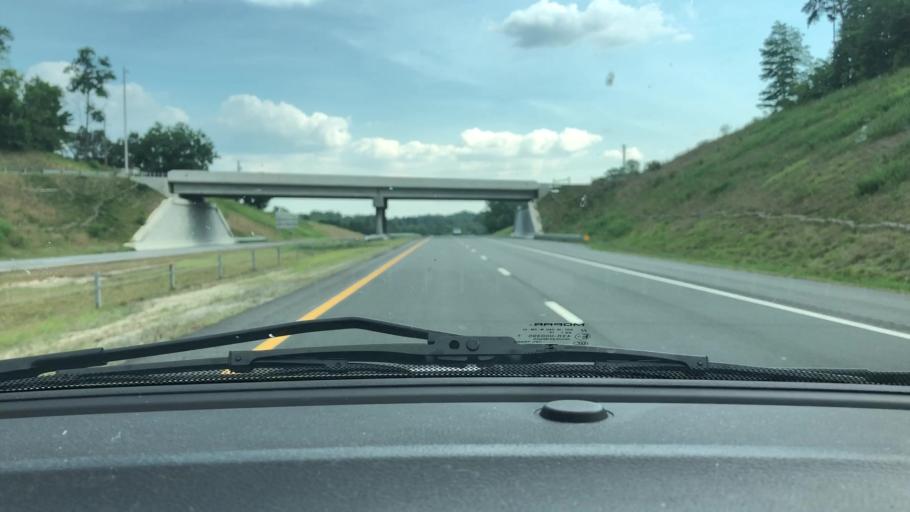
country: US
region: North Carolina
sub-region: Guilford County
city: Summerfield
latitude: 36.1852
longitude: -79.9310
